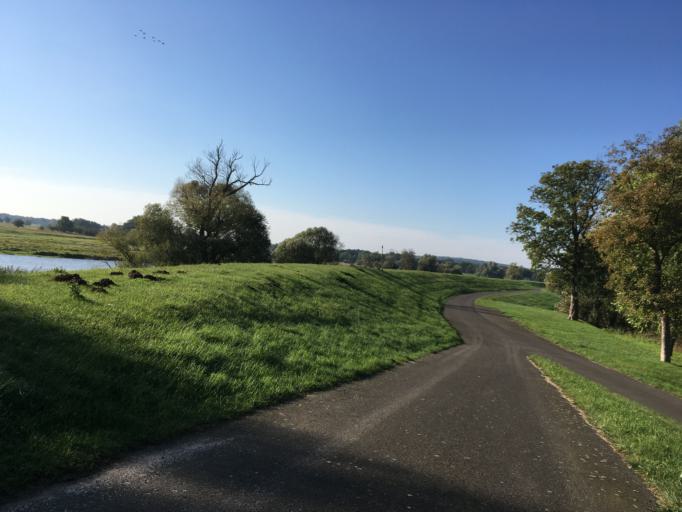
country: DE
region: Brandenburg
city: Reitwein
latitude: 52.5224
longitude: 14.6035
